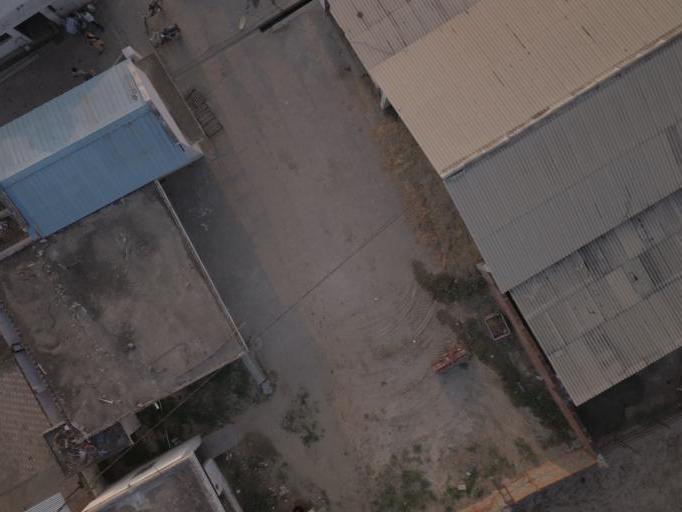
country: IN
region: Punjab
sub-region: Shahid Bhagat Singh Nagar
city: Rahon
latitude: 31.0179
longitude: 76.0934
